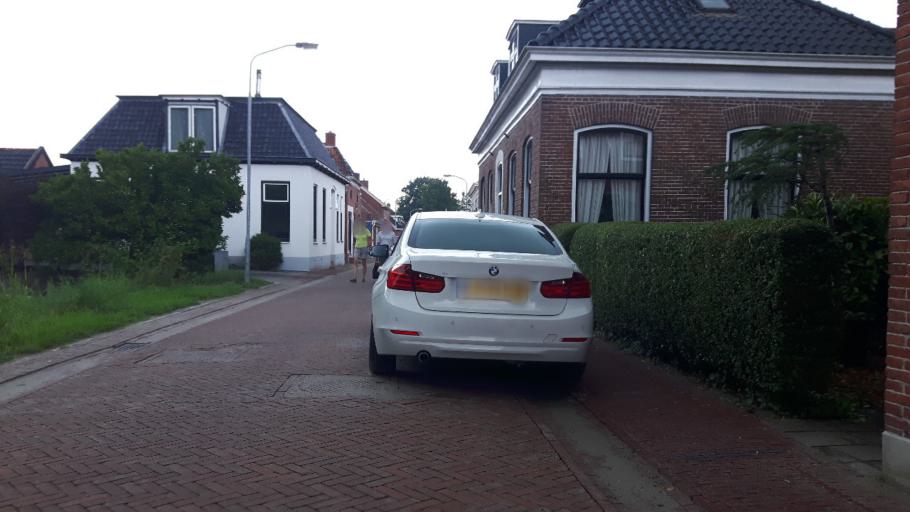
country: NL
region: Groningen
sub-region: Gemeente Bedum
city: Bedum
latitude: 53.3484
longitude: 6.6437
